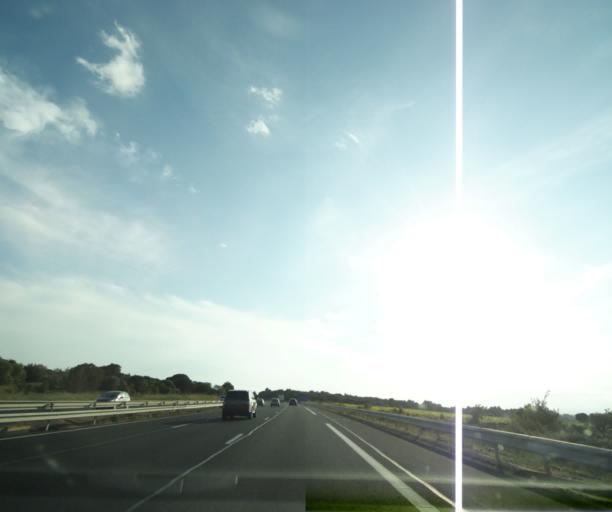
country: FR
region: Languedoc-Roussillon
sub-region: Departement de l'Aude
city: Fleury
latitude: 43.2293
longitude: 3.1079
